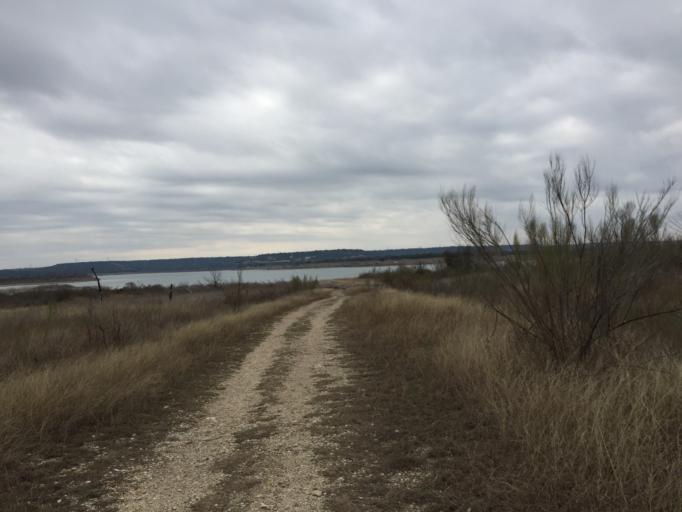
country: US
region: Texas
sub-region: Bell County
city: Nolanville
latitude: 31.0277
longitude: -97.6175
